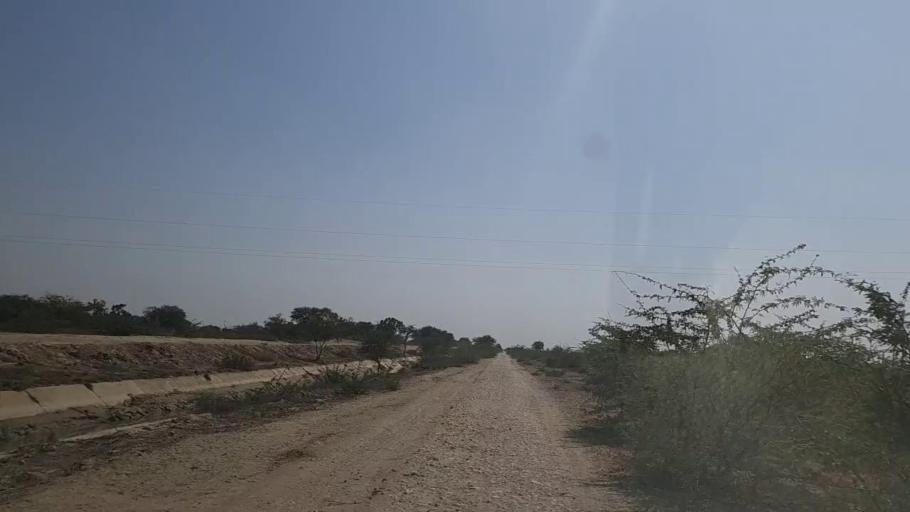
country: PK
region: Sindh
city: Naukot
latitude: 24.6502
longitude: 69.2766
